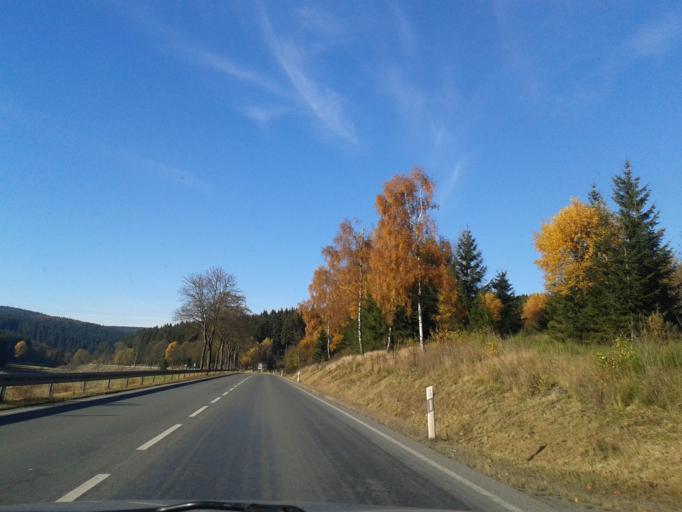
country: DE
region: North Rhine-Westphalia
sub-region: Regierungsbezirk Arnsberg
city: Winterberg
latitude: 51.2205
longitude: 8.5417
